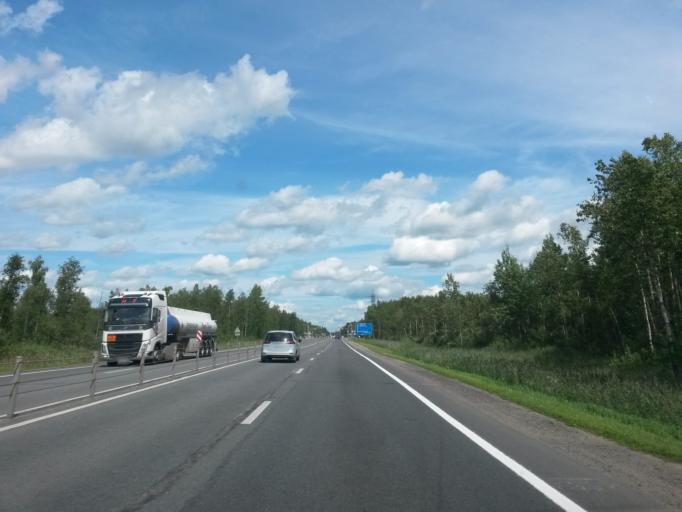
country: RU
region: Jaroslavl
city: Rostov
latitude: 57.2327
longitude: 39.4693
